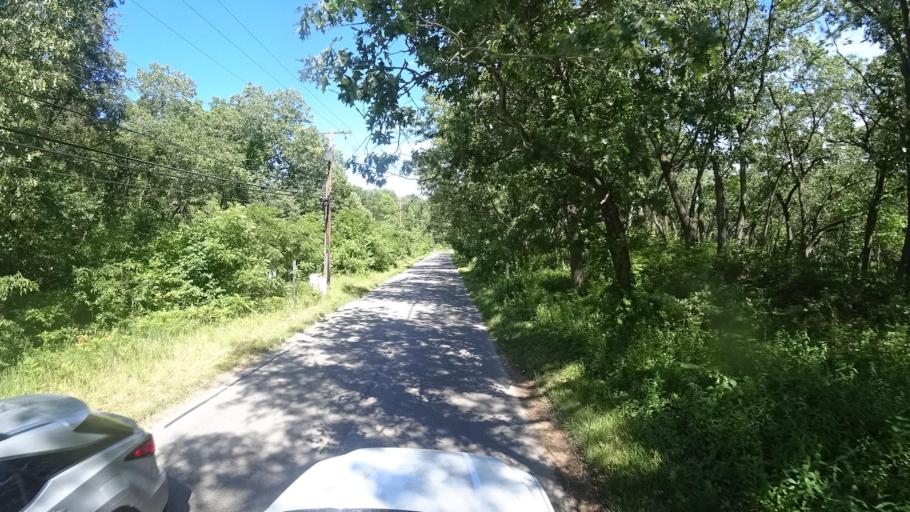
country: US
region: Indiana
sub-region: Porter County
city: Porter
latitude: 41.6548
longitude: -87.0693
